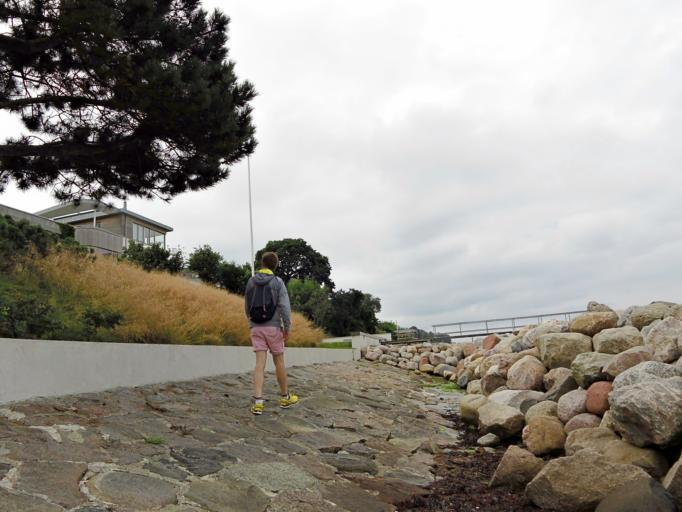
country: DK
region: Capital Region
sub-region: Gentofte Kommune
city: Charlottenlund
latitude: 55.7918
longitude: 12.5928
